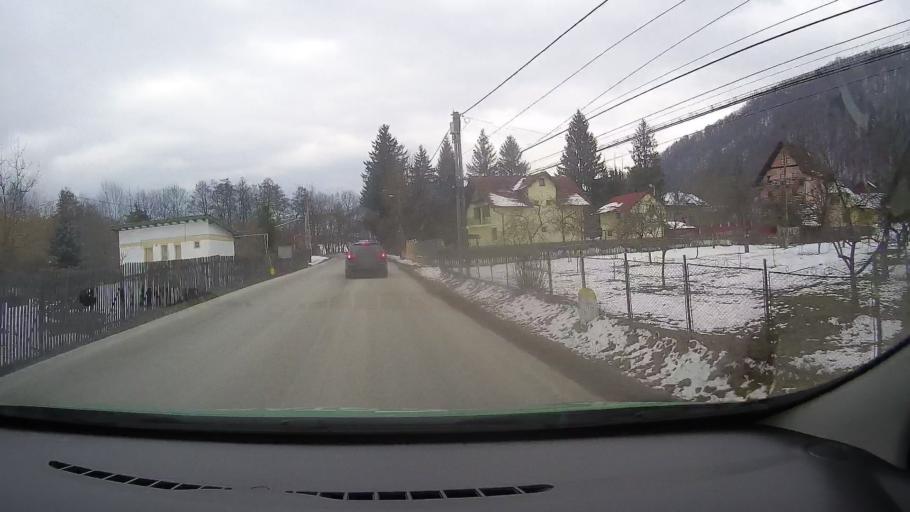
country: RO
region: Brasov
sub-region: Comuna Bran
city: Bran
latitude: 45.5232
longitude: 25.3658
